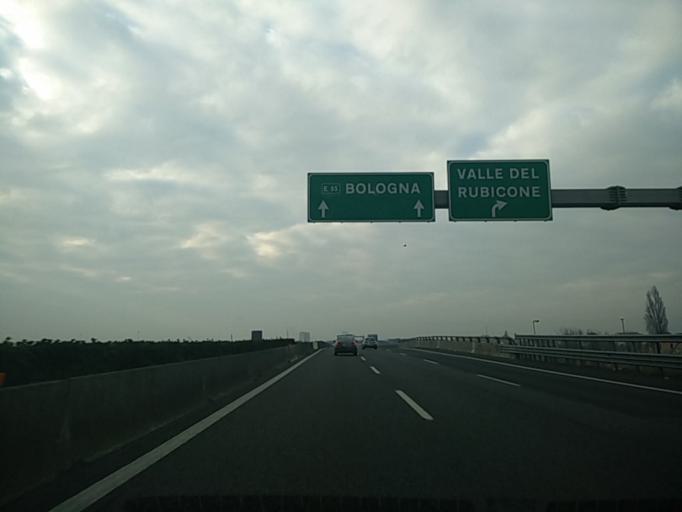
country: IT
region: Emilia-Romagna
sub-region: Forli-Cesena
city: Gatteo-Sant'Angelo
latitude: 44.1181
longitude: 12.4013
